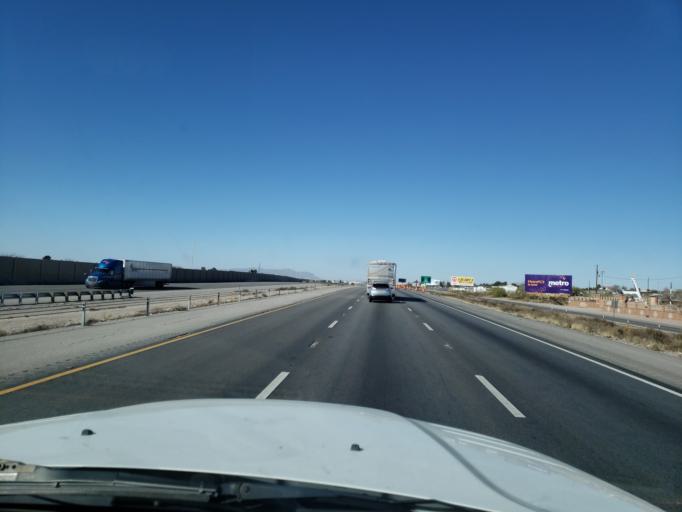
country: US
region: New Mexico
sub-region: Dona Ana County
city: University Park
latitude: 32.2457
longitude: -106.7212
